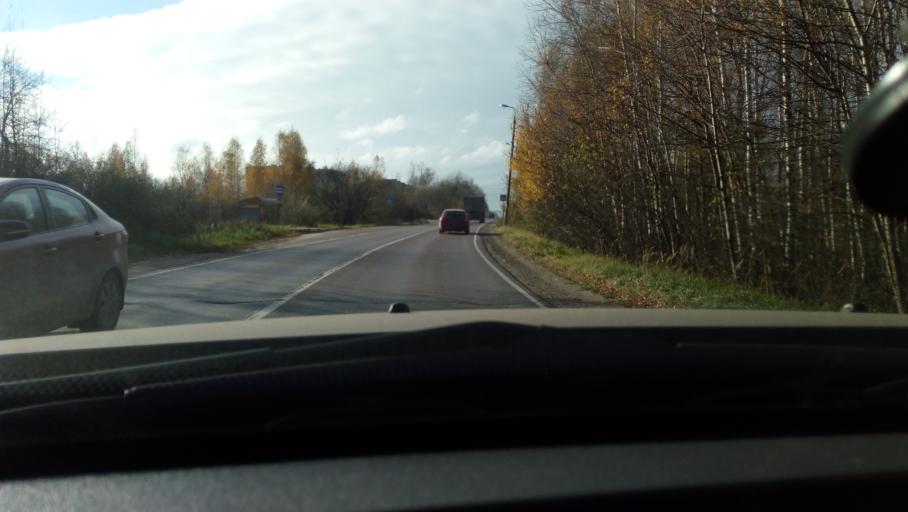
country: RU
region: Moskovskaya
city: Fryazevo
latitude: 55.7181
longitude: 38.4675
